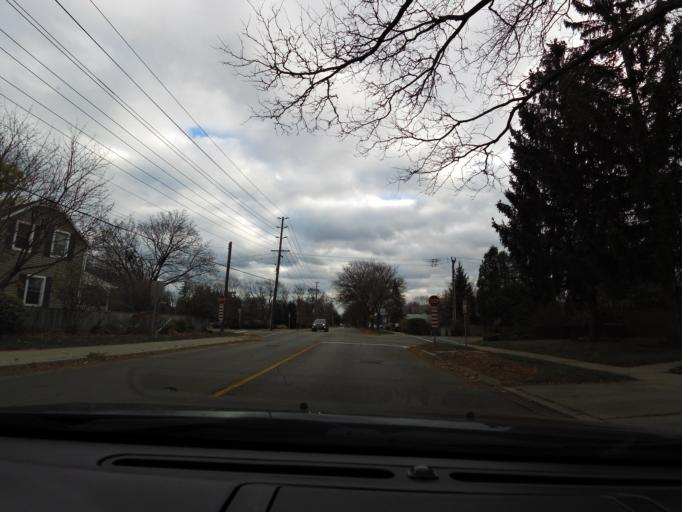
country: CA
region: Ontario
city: Burlington
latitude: 43.3183
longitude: -79.8194
